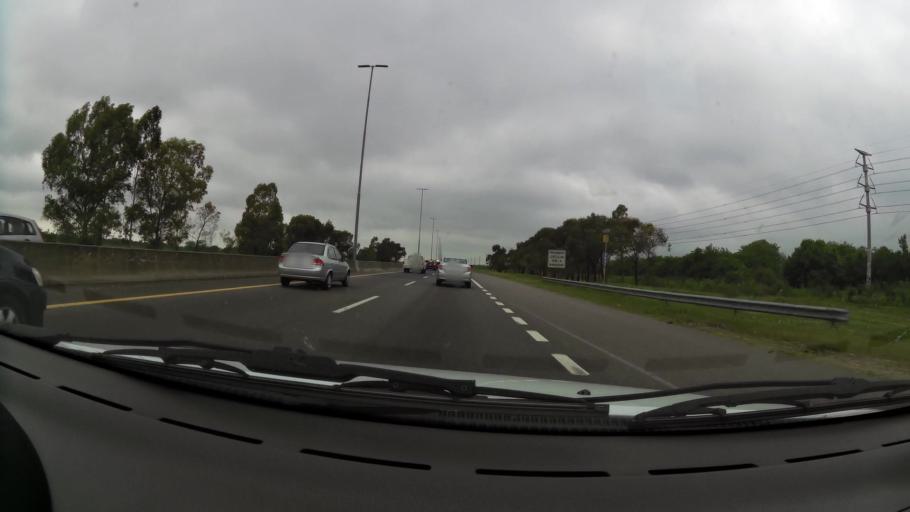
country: AR
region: Buenos Aires
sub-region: Partido de Quilmes
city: Quilmes
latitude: -34.8164
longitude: -58.1092
